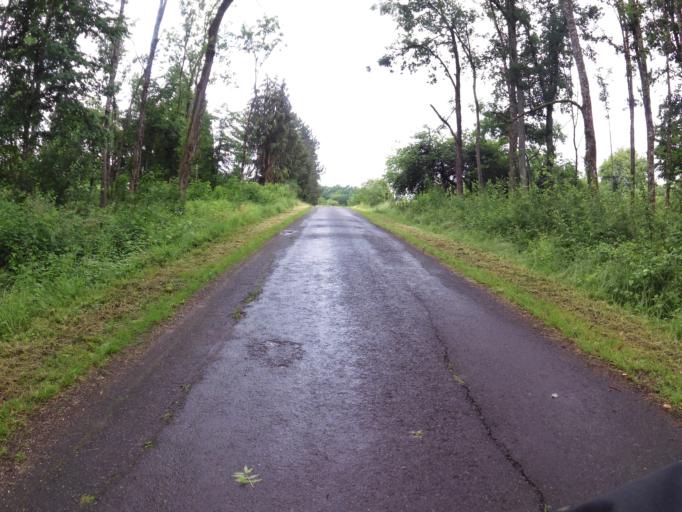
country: FR
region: Champagne-Ardenne
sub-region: Departement de la Marne
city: Sermaize-les-Bains
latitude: 48.7751
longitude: 4.9227
